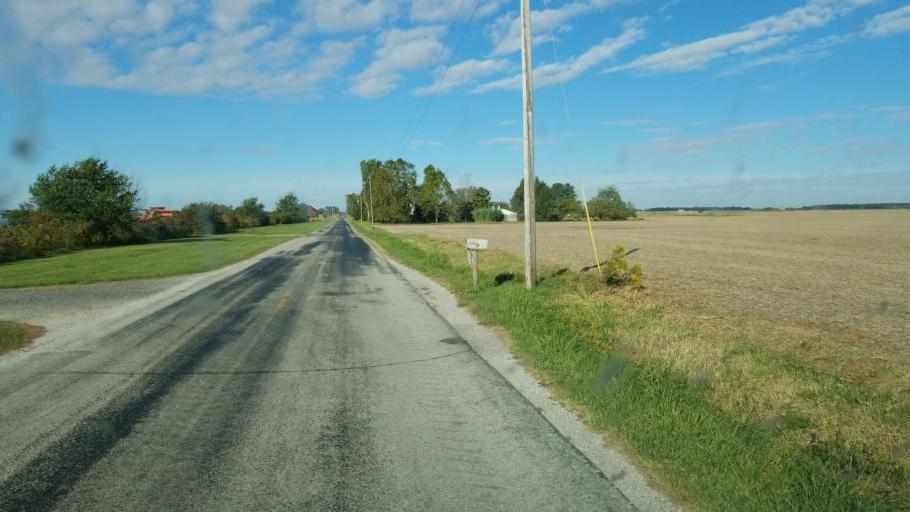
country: US
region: Ohio
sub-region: Crawford County
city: Bucyrus
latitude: 40.6886
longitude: -83.0272
